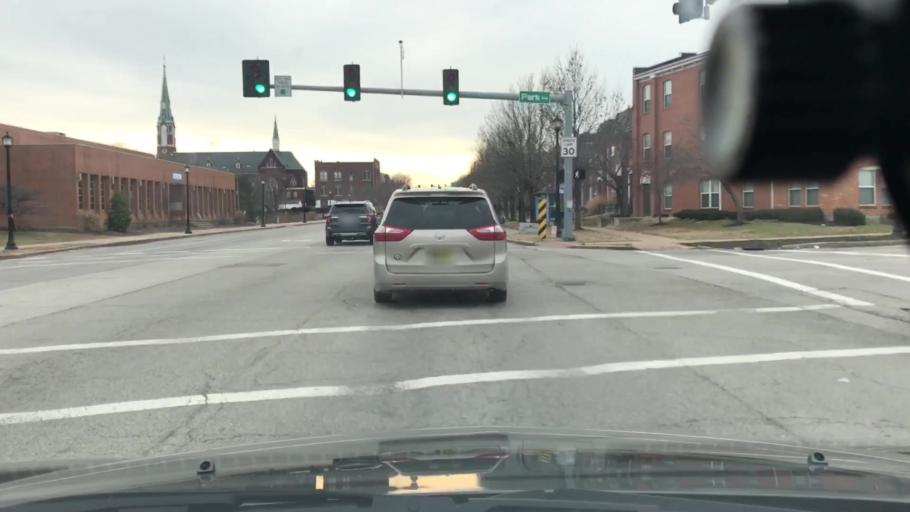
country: US
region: Missouri
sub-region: City of Saint Louis
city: St. Louis
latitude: 38.6149
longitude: -90.2043
